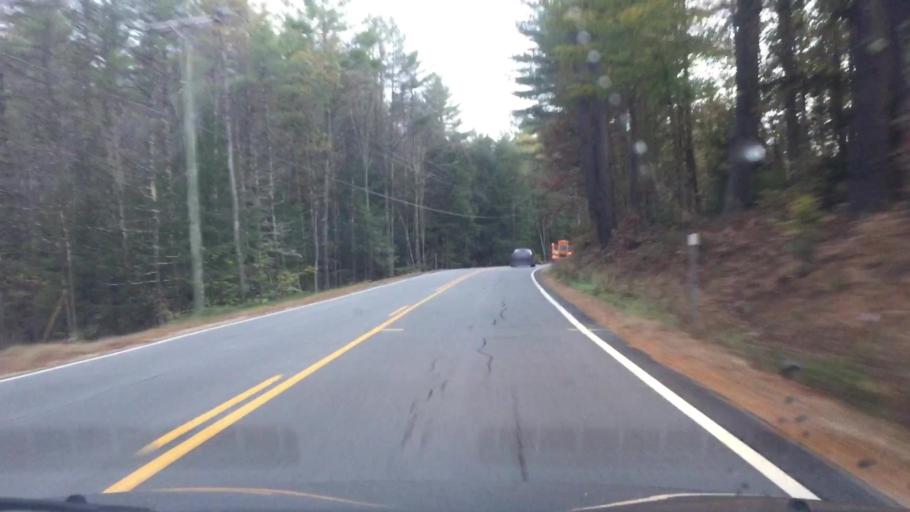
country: US
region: New Hampshire
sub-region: Cheshire County
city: Swanzey
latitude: 42.8398
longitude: -72.2787
